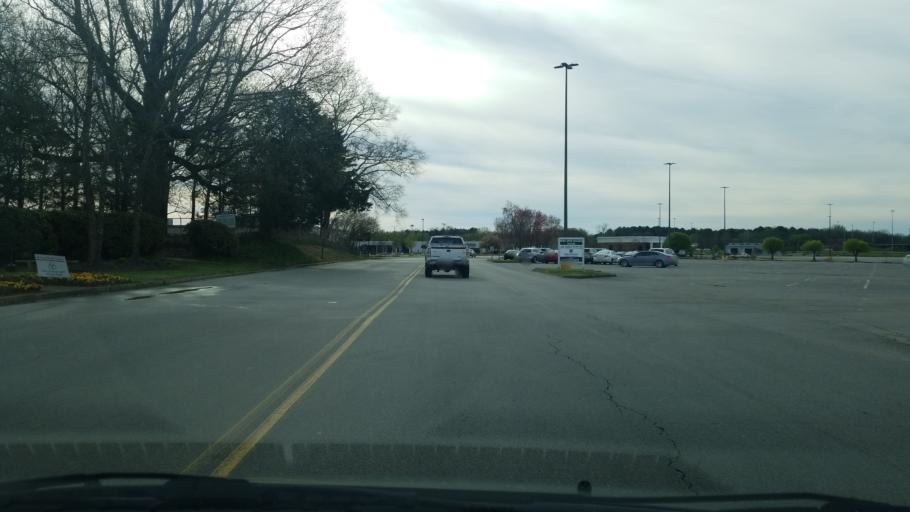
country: US
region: Tennessee
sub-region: Hamilton County
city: East Ridge
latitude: 35.0101
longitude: -85.2139
